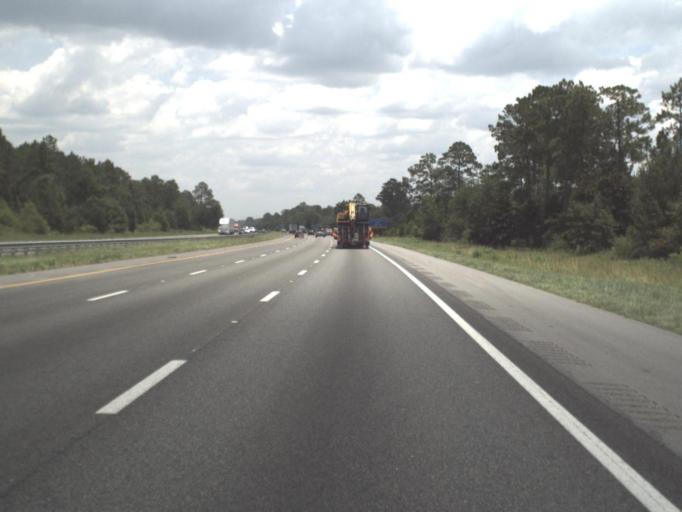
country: US
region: Georgia
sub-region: Echols County
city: Statenville
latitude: 30.6243
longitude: -83.1697
